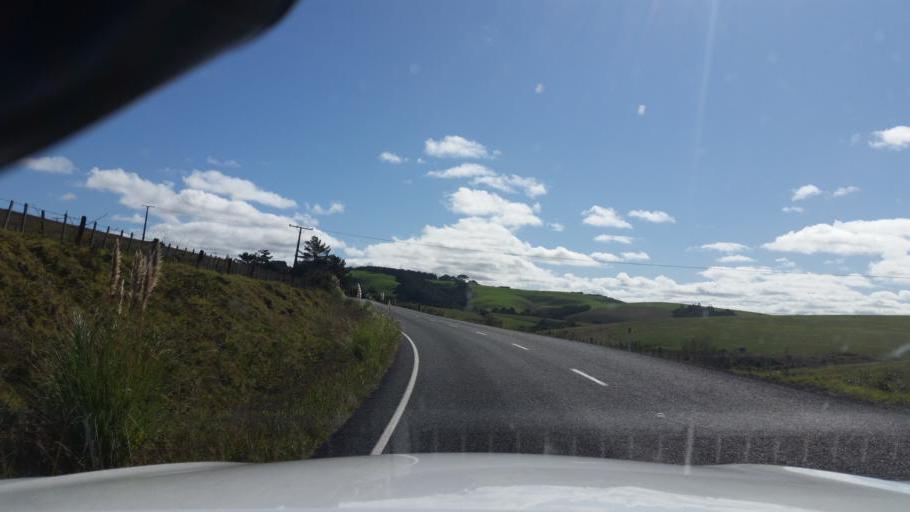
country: NZ
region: Auckland
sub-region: Auckland
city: Wellsford
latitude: -36.2140
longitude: 174.1827
